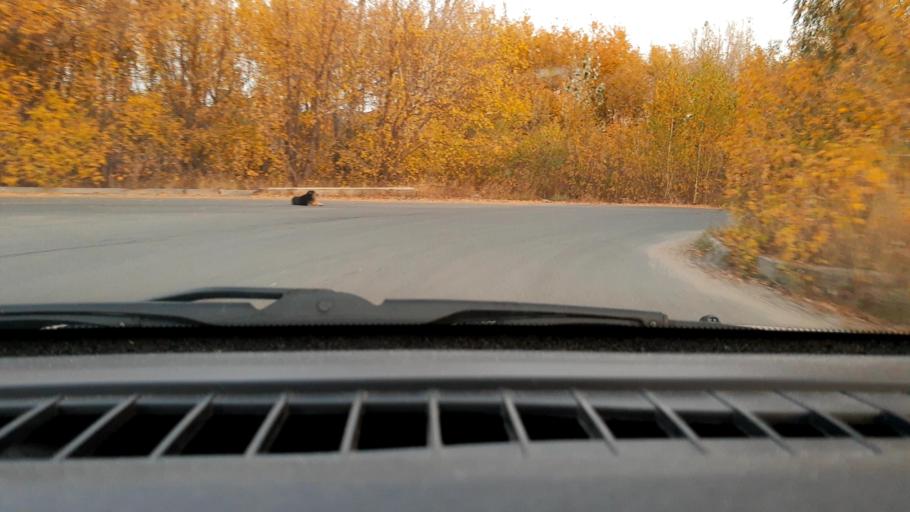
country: RU
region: Nizjnij Novgorod
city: Nizhniy Novgorod
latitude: 56.2341
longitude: 43.9048
